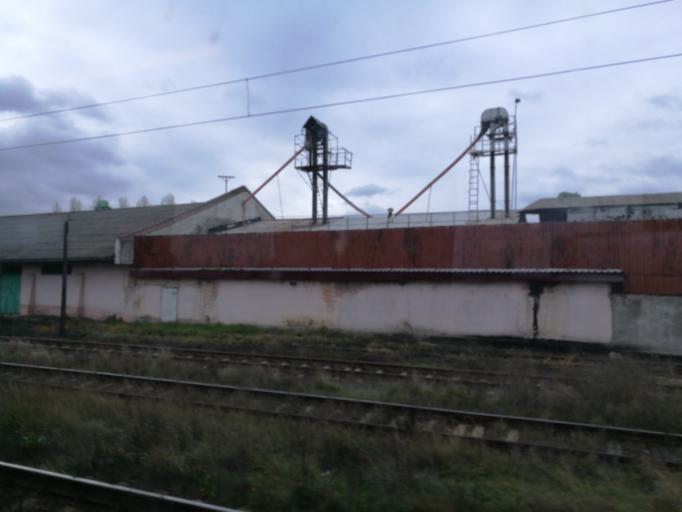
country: RO
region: Iasi
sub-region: Municipiul Pascani
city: Pascani
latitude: 47.2630
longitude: 26.7207
